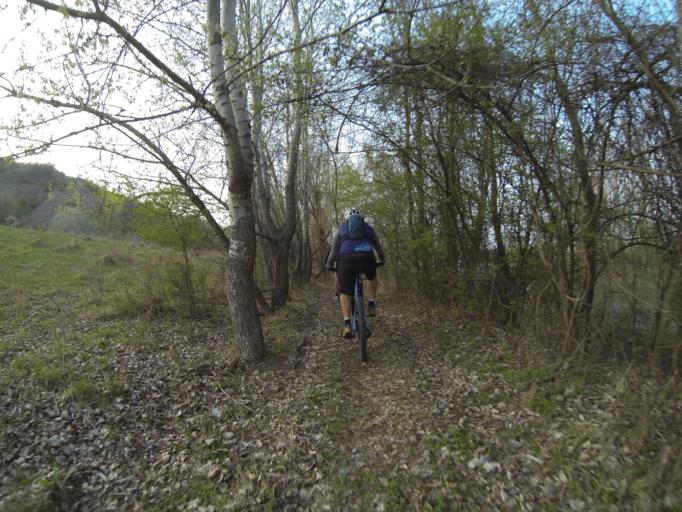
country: RO
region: Dolj
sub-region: Comuna Bucovat
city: Bucovat
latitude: 44.2817
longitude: 23.7588
